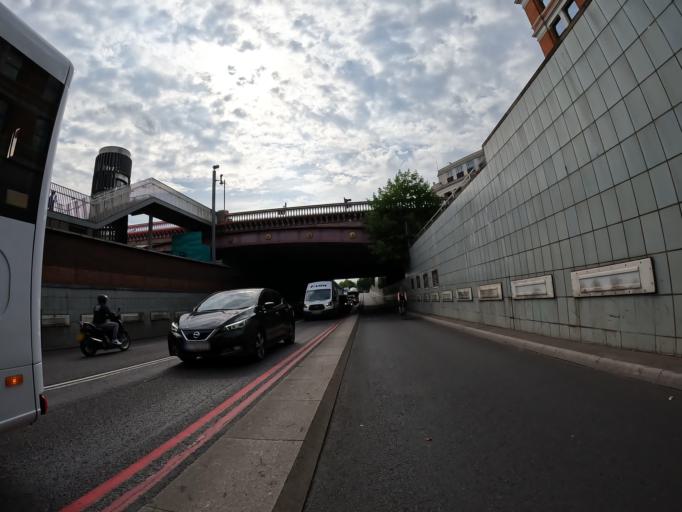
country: GB
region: England
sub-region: Greater London
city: Barnsbury
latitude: 51.5469
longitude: -0.1127
